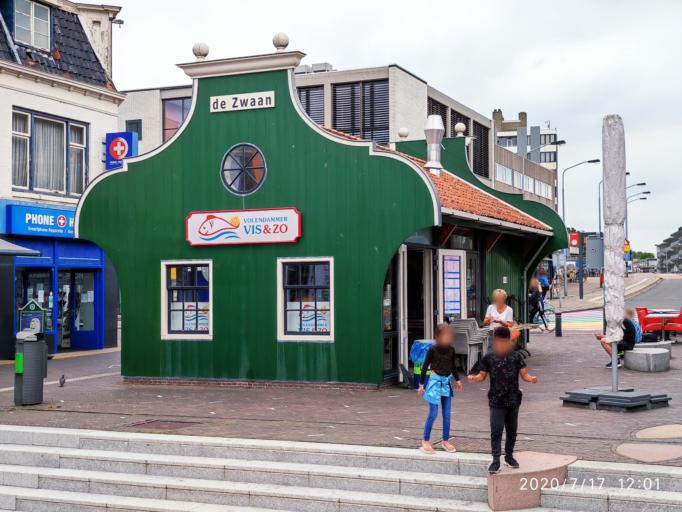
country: NL
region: North Holland
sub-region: Gemeente Zaanstad
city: Zaandam
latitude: 52.4398
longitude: 4.8230
